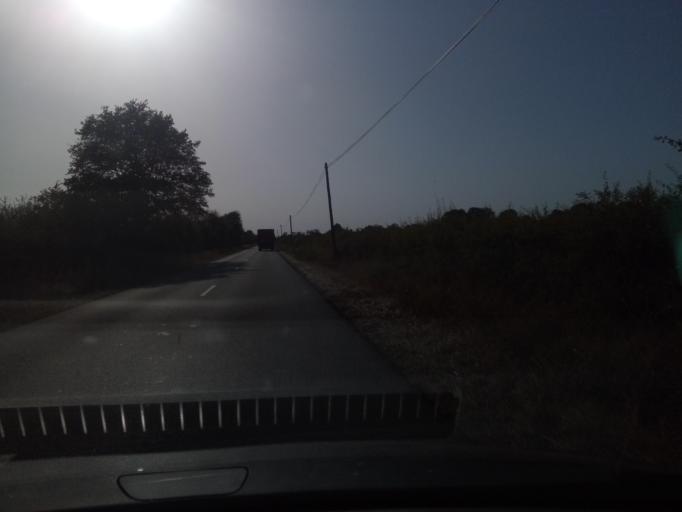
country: FR
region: Poitou-Charentes
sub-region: Departement de la Vienne
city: Montmorillon
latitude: 46.4401
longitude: 0.9419
